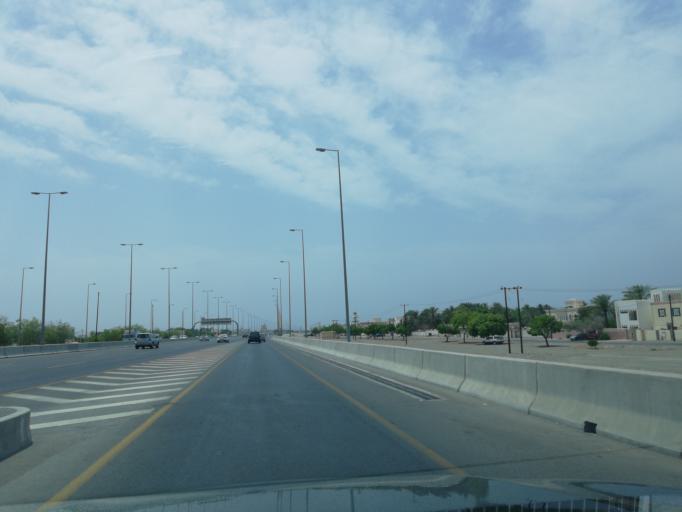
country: OM
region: Muhafazat Masqat
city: As Sib al Jadidah
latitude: 23.6665
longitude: 58.1593
